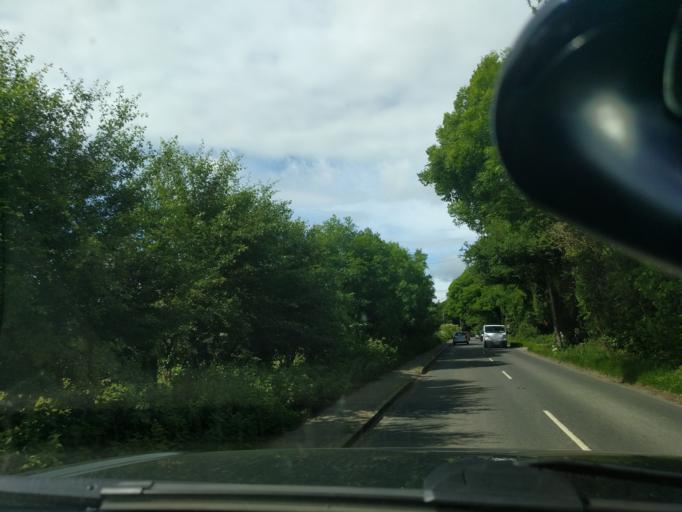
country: GB
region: England
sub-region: Wiltshire
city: Bradford-on-Avon
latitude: 51.3604
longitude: -2.2375
